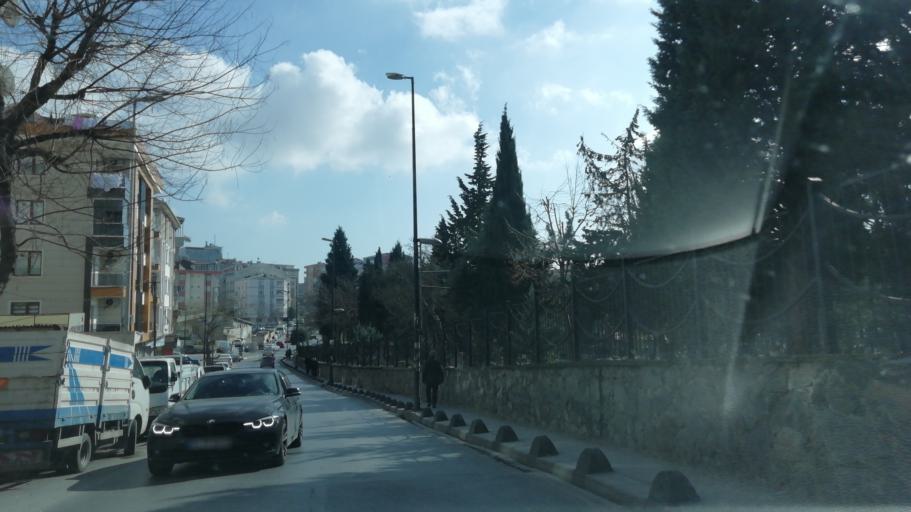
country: TR
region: Istanbul
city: Bahcelievler
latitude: 41.0159
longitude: 28.8381
